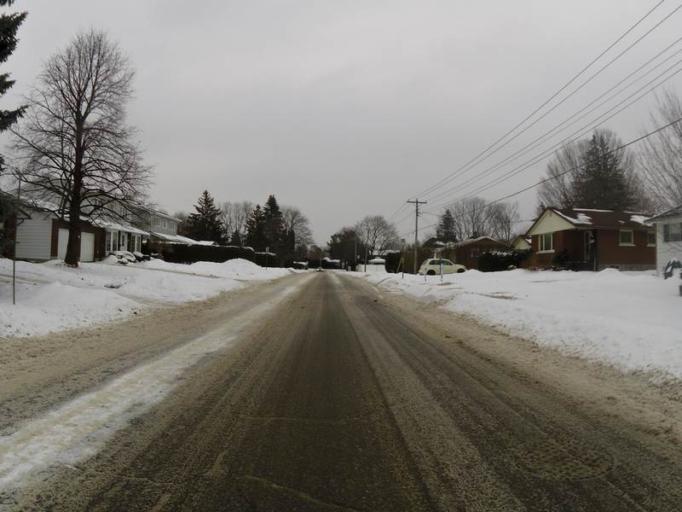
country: CA
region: Ontario
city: Bells Corners
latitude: 45.3457
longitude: -75.7525
